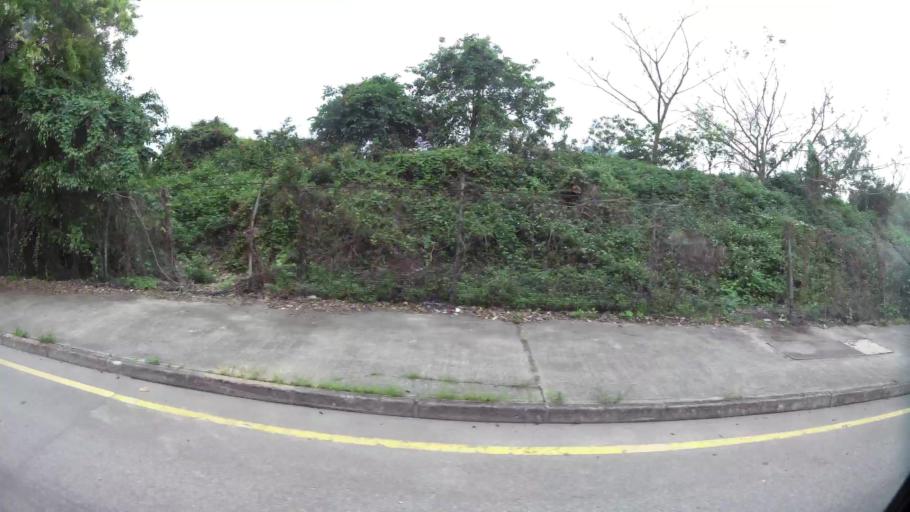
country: MO
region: Macau
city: Macau
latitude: 22.1380
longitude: 113.5592
